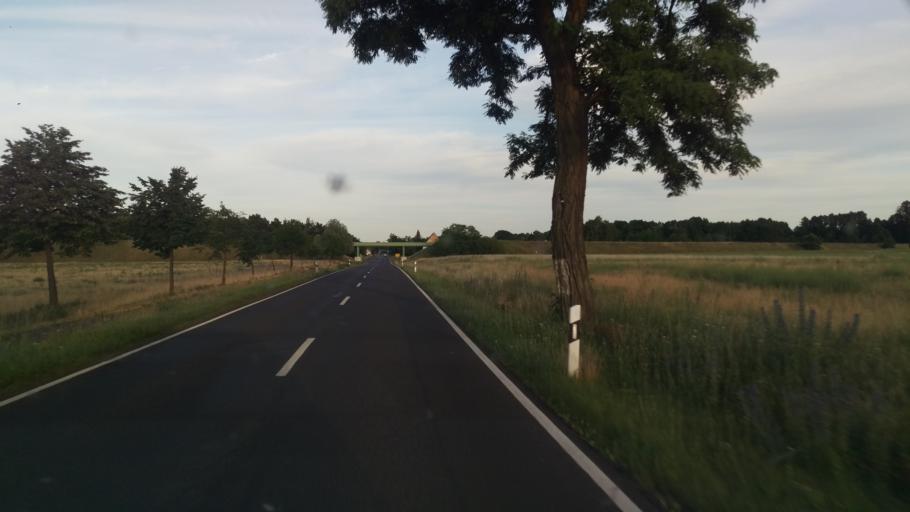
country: DE
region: Brandenburg
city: Vogelsang
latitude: 52.1877
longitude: 14.6540
